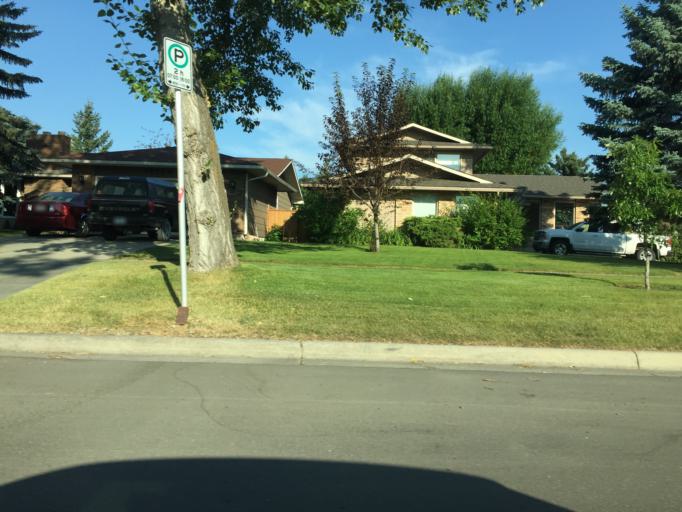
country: CA
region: Alberta
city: Calgary
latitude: 50.9384
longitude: -114.0644
